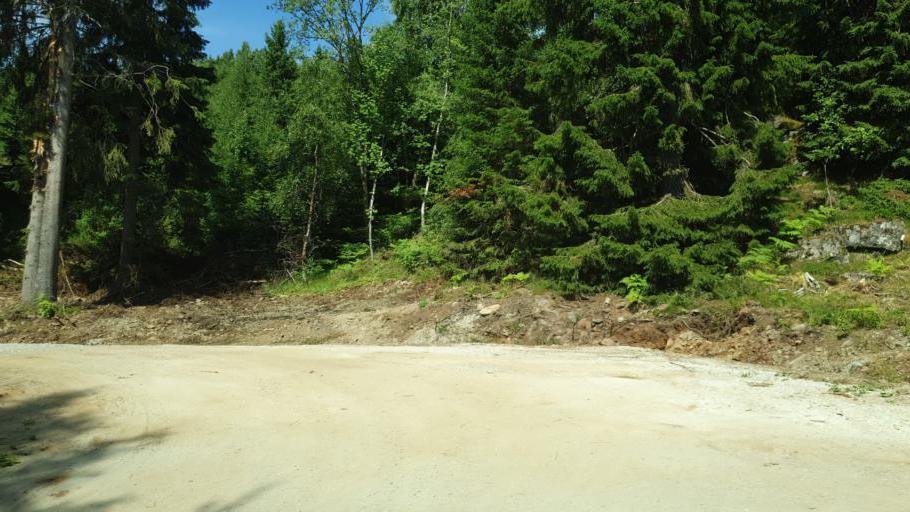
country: NO
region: Nord-Trondelag
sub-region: Leksvik
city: Leksvik
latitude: 63.6806
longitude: 10.6630
